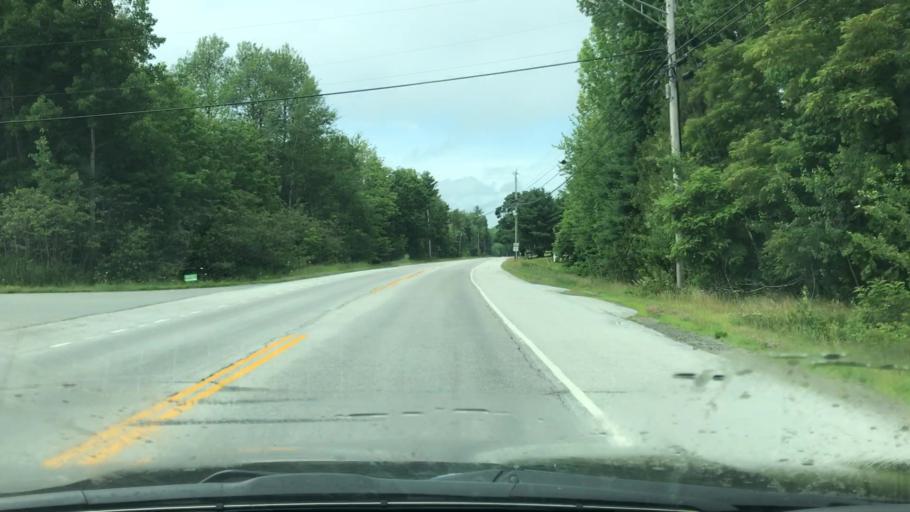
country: US
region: Maine
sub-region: Waldo County
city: Northport
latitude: 44.3378
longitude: -68.9617
